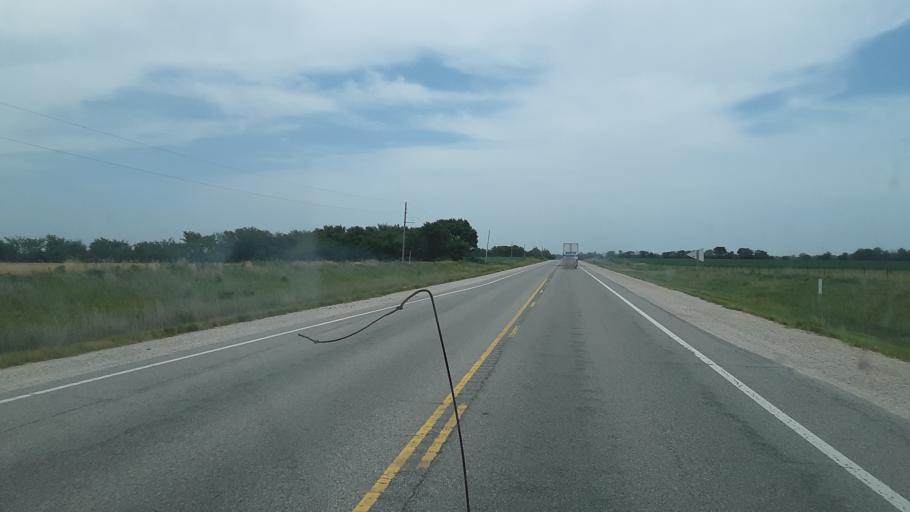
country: US
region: Kansas
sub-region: Allen County
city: Iola
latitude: 37.9217
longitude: -95.2241
